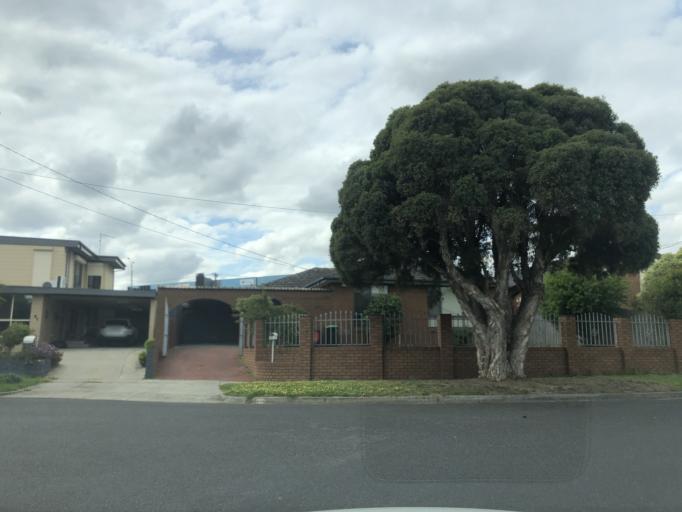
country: AU
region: Victoria
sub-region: Greater Dandenong
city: Noble Park North
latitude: -37.9386
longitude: 145.1934
